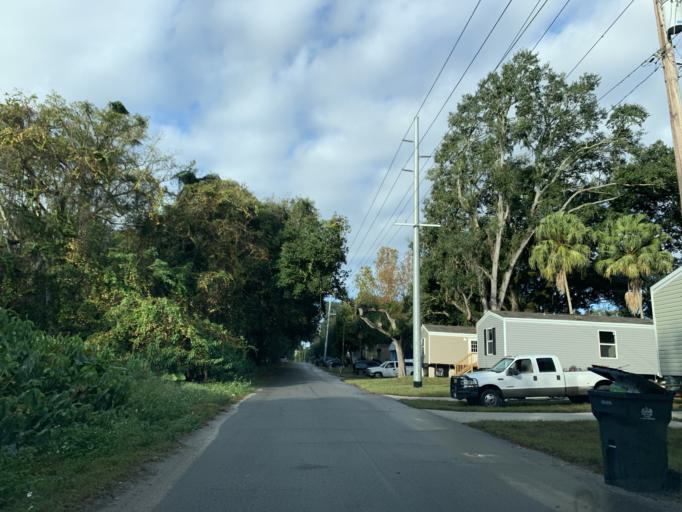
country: US
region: Florida
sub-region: Hillsborough County
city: Mango
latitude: 27.9851
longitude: -82.3198
